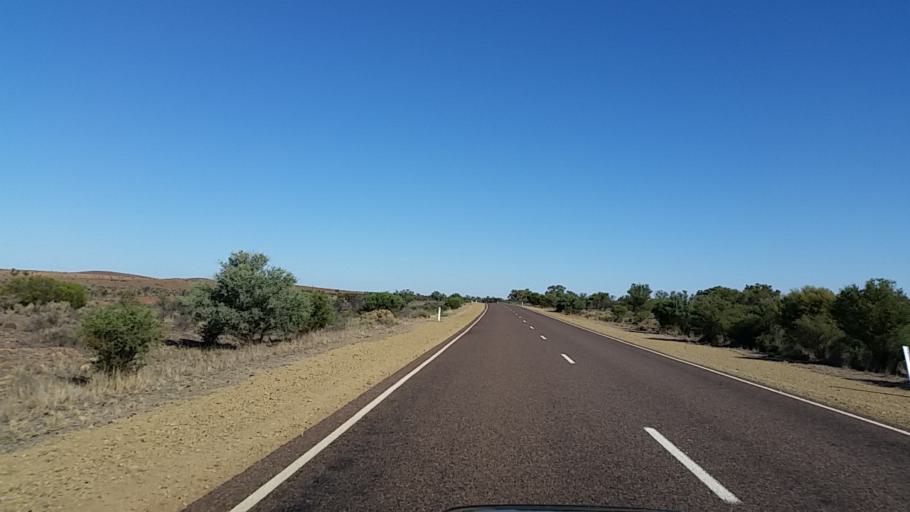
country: AU
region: South Australia
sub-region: Flinders Ranges
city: Quorn
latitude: -32.3646
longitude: 138.4966
